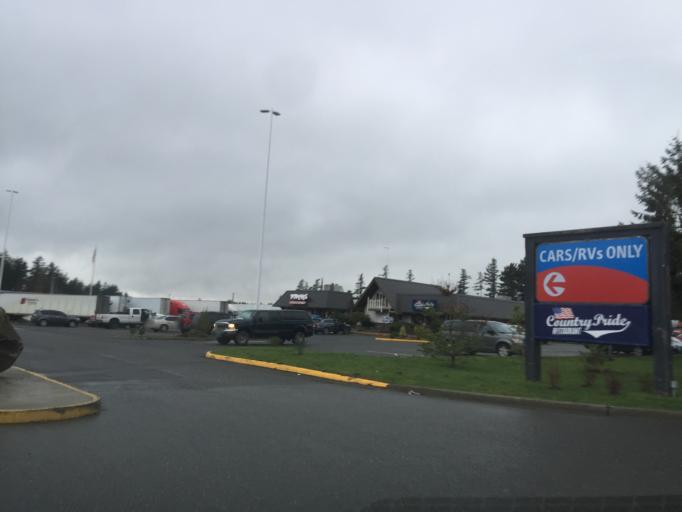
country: US
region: Washington
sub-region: King County
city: Tanner
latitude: 47.4678
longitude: -121.7162
